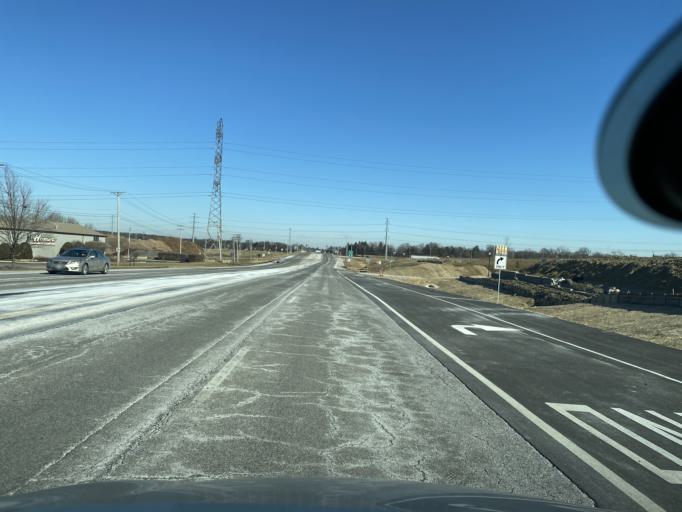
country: US
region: Illinois
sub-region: Cook County
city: Lemont
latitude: 41.6315
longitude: -88.0159
